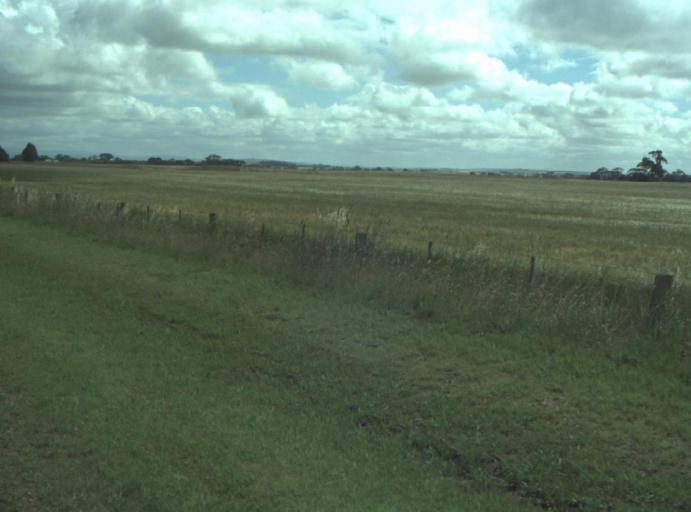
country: AU
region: Victoria
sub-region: Greater Geelong
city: Lara
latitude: -37.8653
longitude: 144.3509
